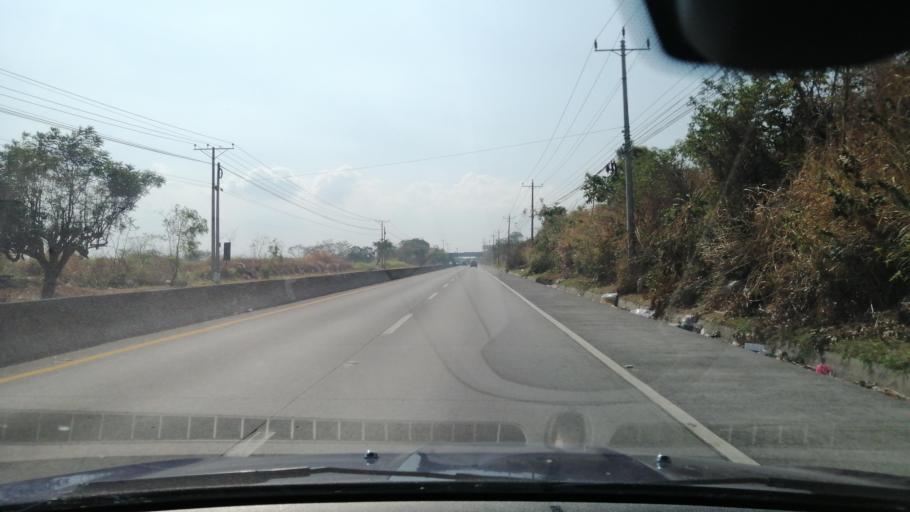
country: SV
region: San Salvador
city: Apopa
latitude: 13.7897
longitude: -89.2206
